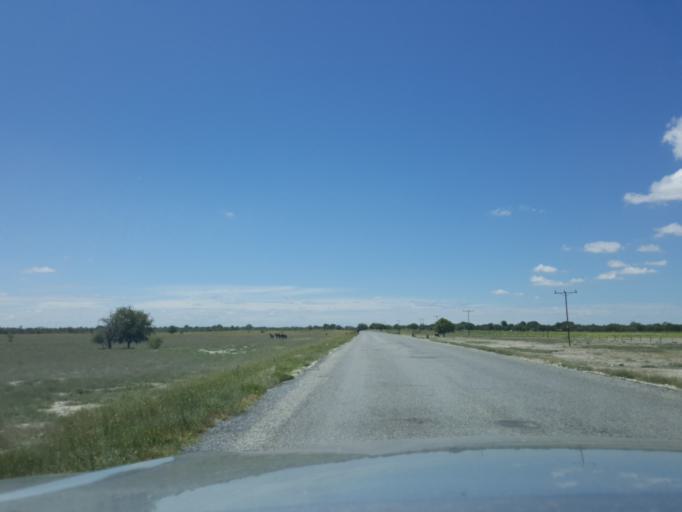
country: BW
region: Central
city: Nata
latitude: -20.1586
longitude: 25.8438
